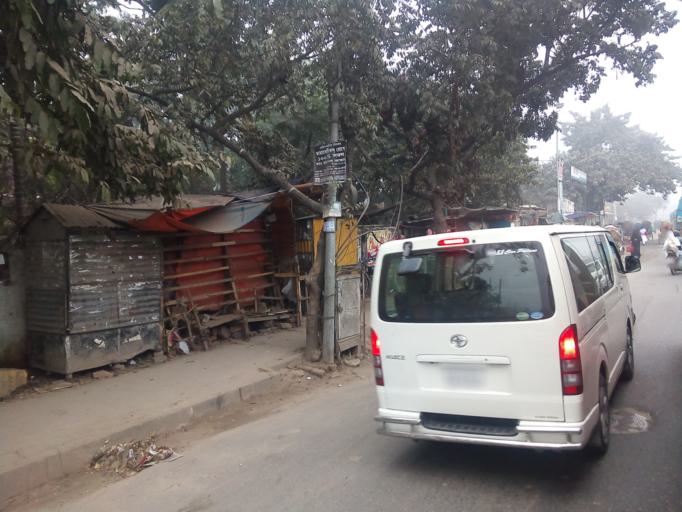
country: BD
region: Dhaka
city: Azimpur
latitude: 23.7830
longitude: 90.3786
